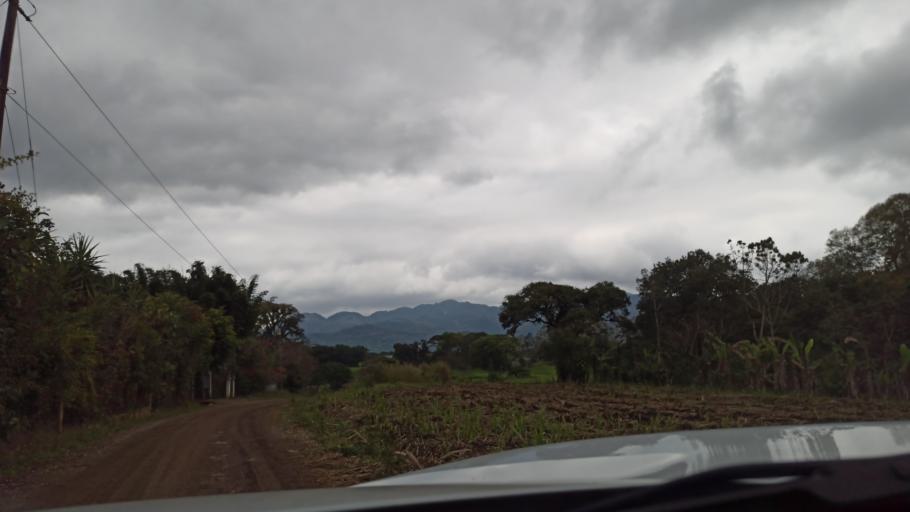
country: MX
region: Veracruz
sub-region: Chocaman
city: San Jose Neria
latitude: 18.9845
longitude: -97.0074
